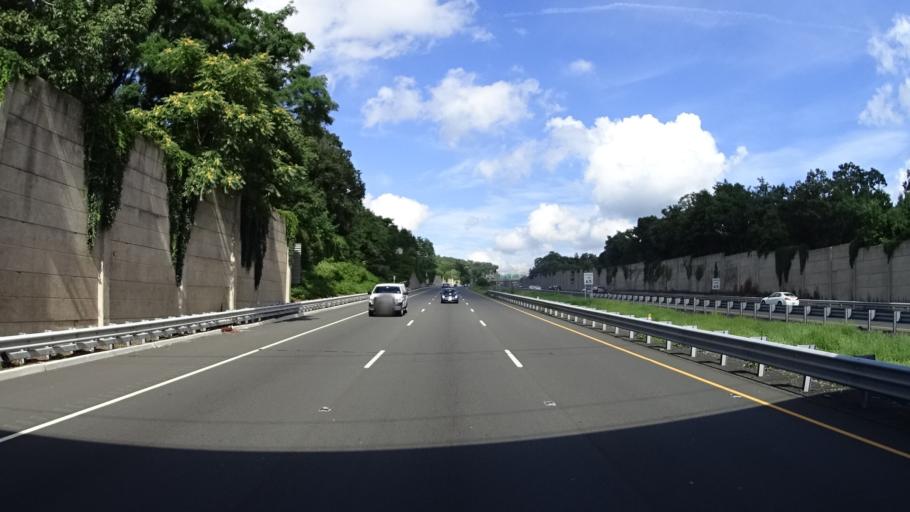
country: US
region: New Jersey
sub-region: Union County
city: Summit
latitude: 40.7230
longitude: -74.3392
